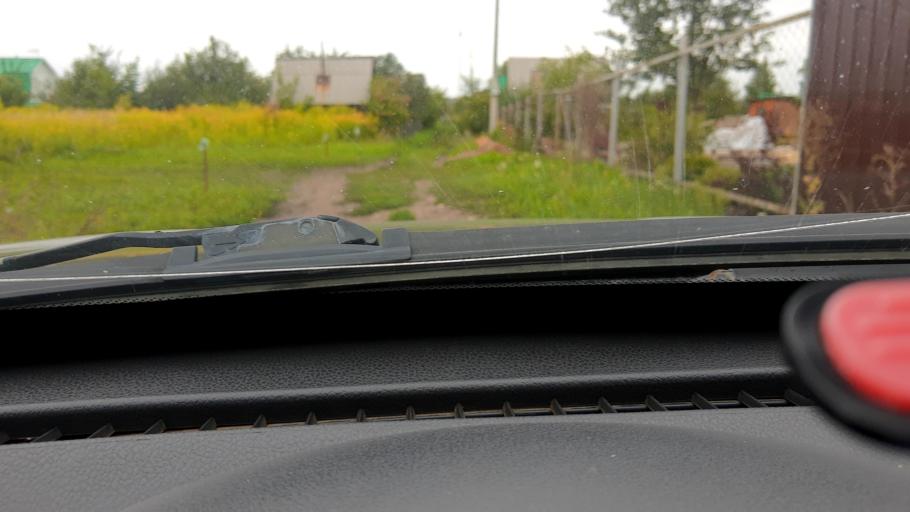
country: RU
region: Bashkortostan
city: Kabakovo
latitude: 54.7196
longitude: 56.1784
